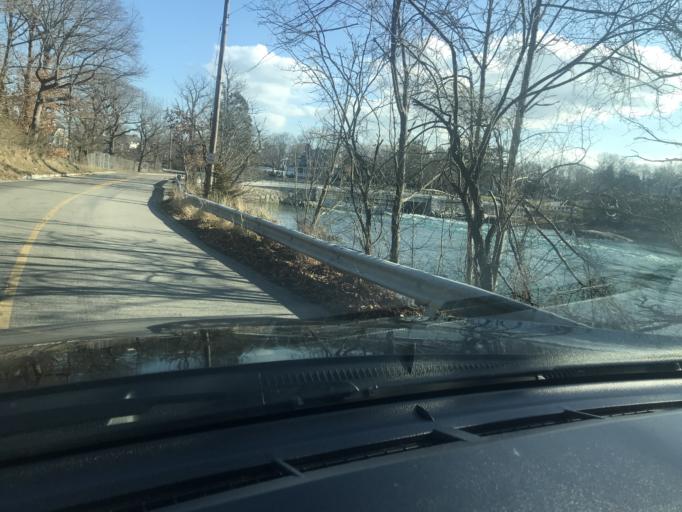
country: US
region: Massachusetts
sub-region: Norfolk County
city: Cohasset
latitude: 42.2531
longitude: -70.7961
